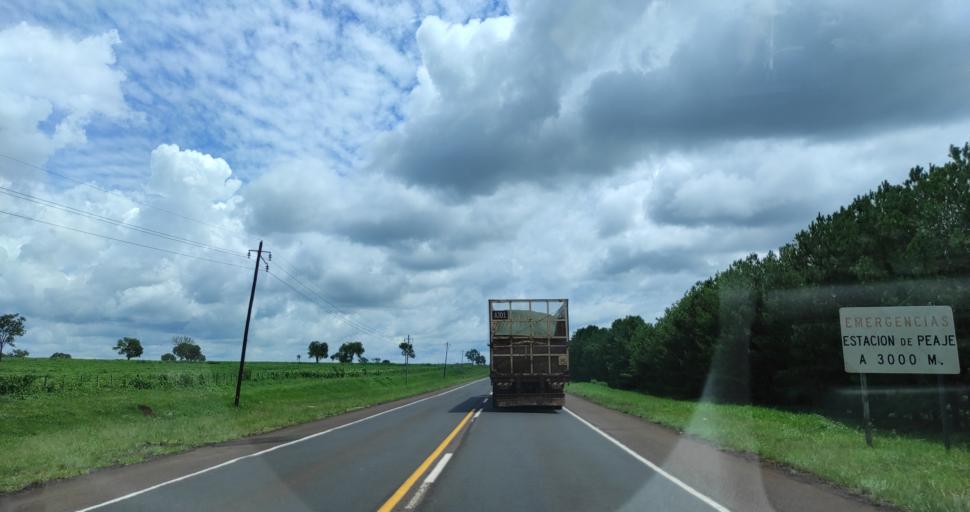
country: AR
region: Misiones
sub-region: Departamento de Apostoles
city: San Jose
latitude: -27.6686
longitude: -55.8158
